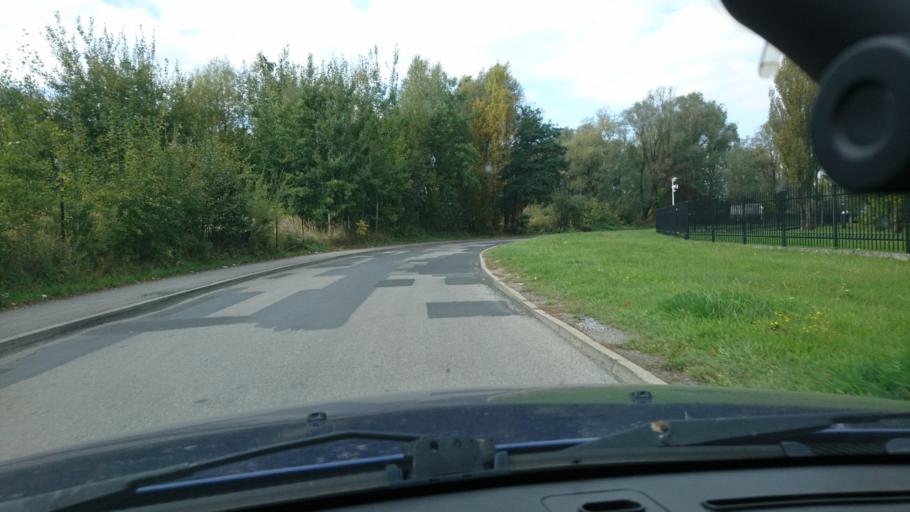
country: PL
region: Silesian Voivodeship
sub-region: Bielsko-Biala
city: Bielsko-Biala
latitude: 49.8563
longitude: 19.0379
